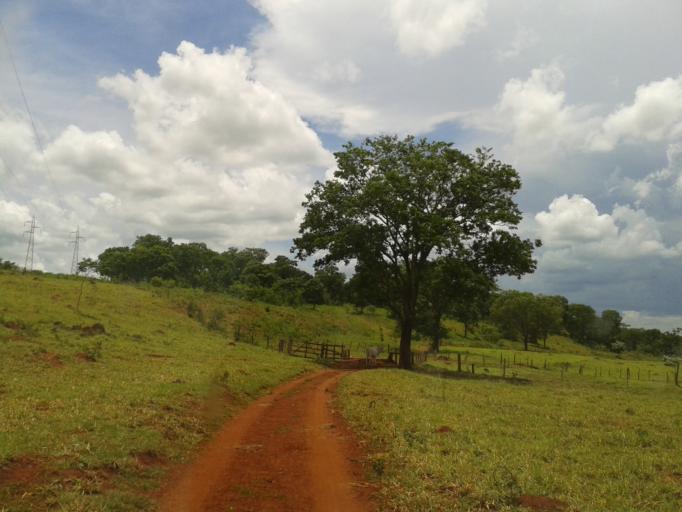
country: BR
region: Minas Gerais
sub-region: Centralina
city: Centralina
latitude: -18.6985
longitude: -49.2326
